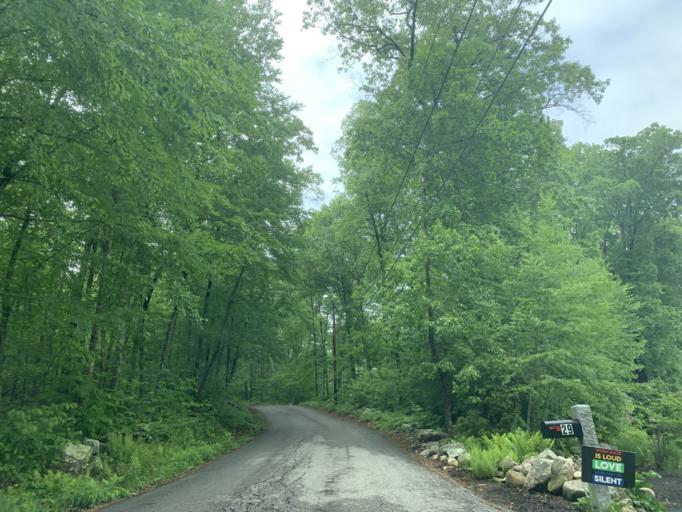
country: US
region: Massachusetts
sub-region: Worcester County
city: Upton
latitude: 42.1939
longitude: -71.6298
